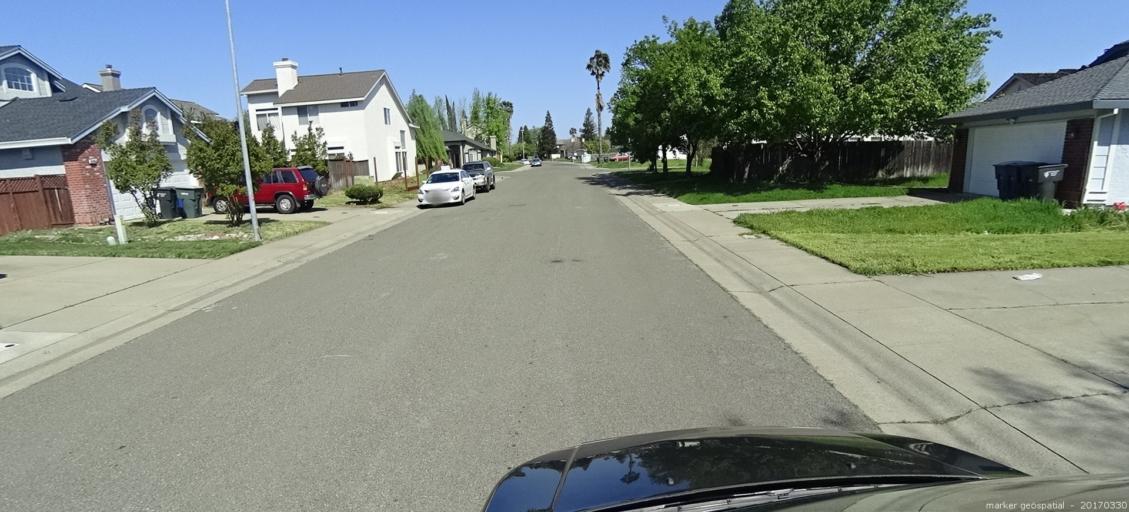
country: US
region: California
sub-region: Sacramento County
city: Laguna
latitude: 38.4416
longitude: -121.4203
